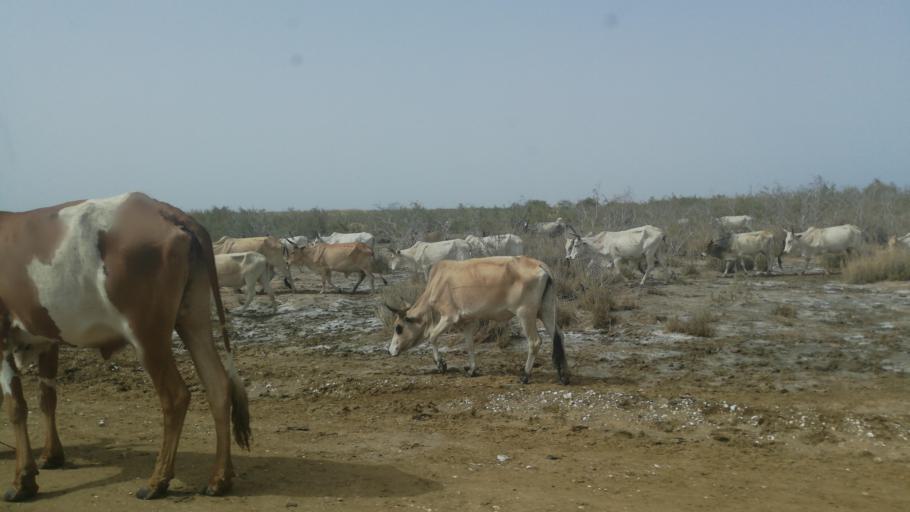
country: SN
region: Saint-Louis
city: Saint-Louis
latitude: 16.0655
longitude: -16.3208
